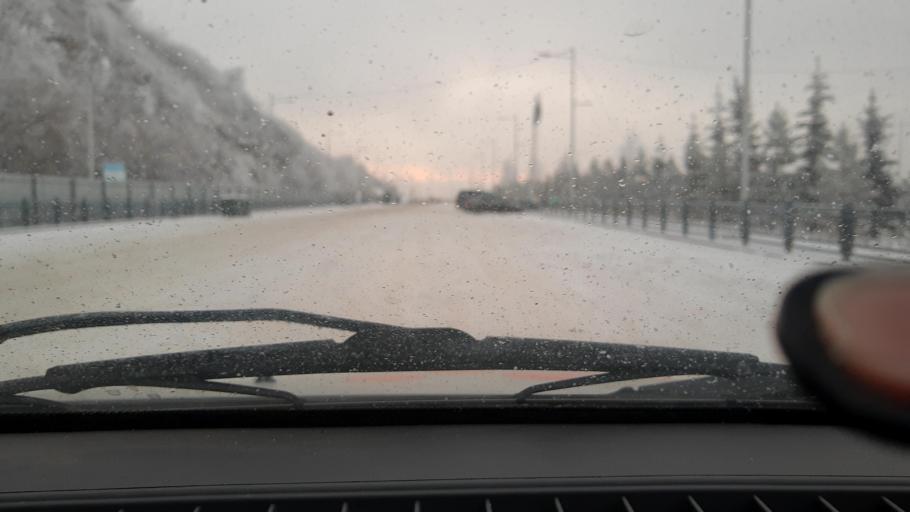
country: RU
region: Bashkortostan
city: Ufa
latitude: 54.7173
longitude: 55.9240
